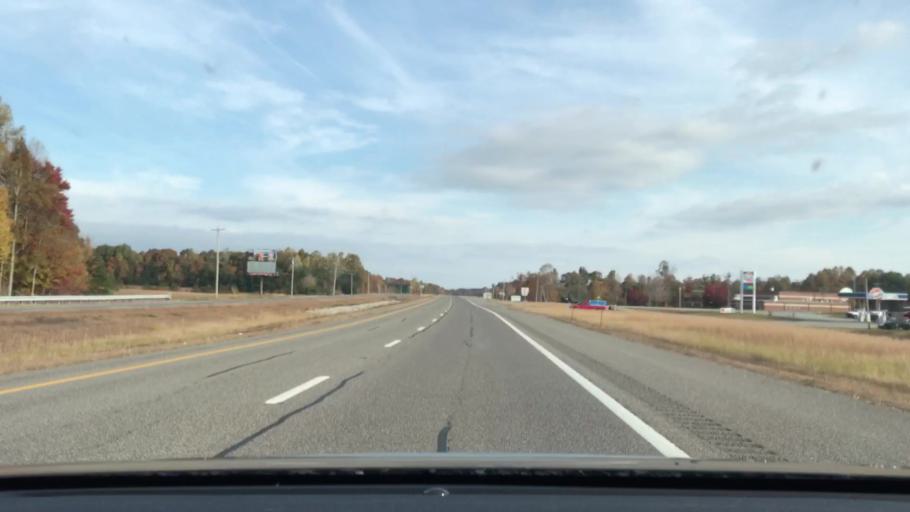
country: US
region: Tennessee
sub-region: Fentress County
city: Jamestown
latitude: 36.3555
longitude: -84.9494
